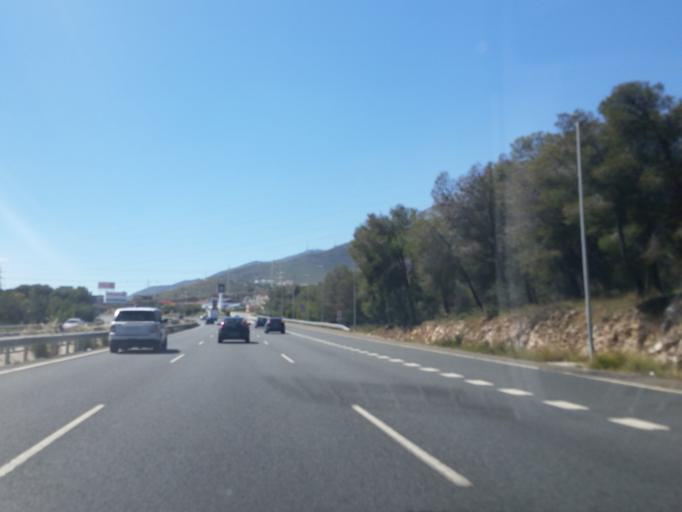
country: ES
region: Andalusia
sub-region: Provincia de Malaga
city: Torremolinos
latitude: 36.6148
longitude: -4.5233
